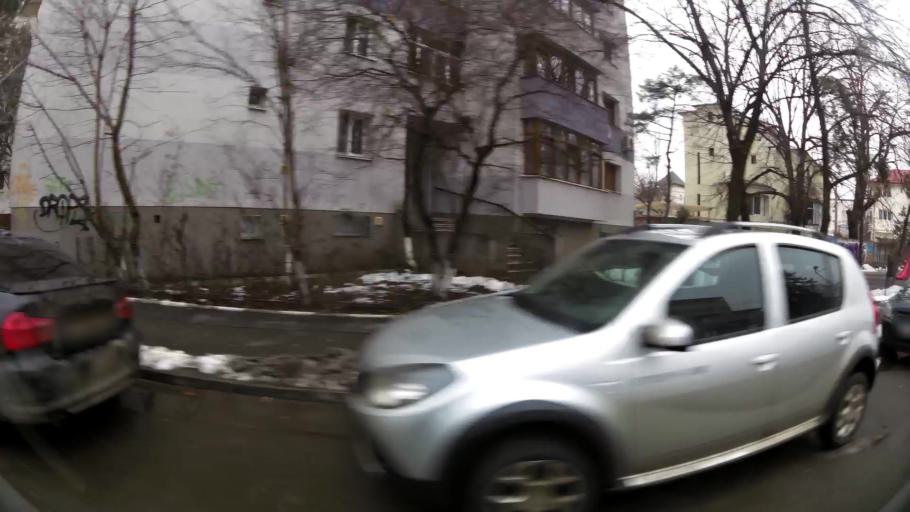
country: RO
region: Ilfov
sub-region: Comuna Chiajna
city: Rosu
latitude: 44.4702
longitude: 26.0586
